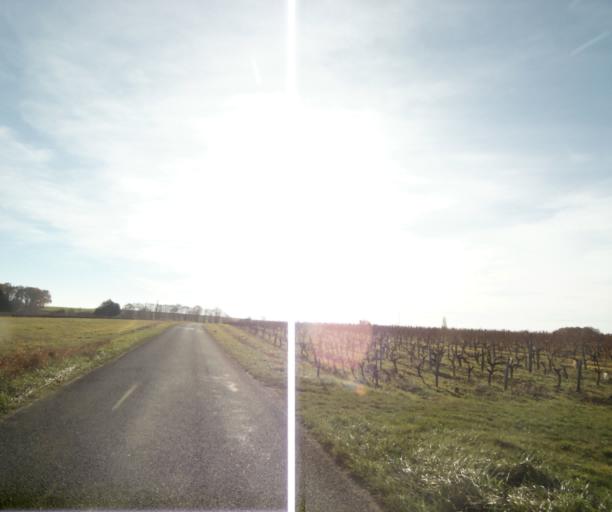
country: FR
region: Poitou-Charentes
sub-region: Departement de la Charente-Maritime
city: Chaniers
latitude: 45.7342
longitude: -0.5487
